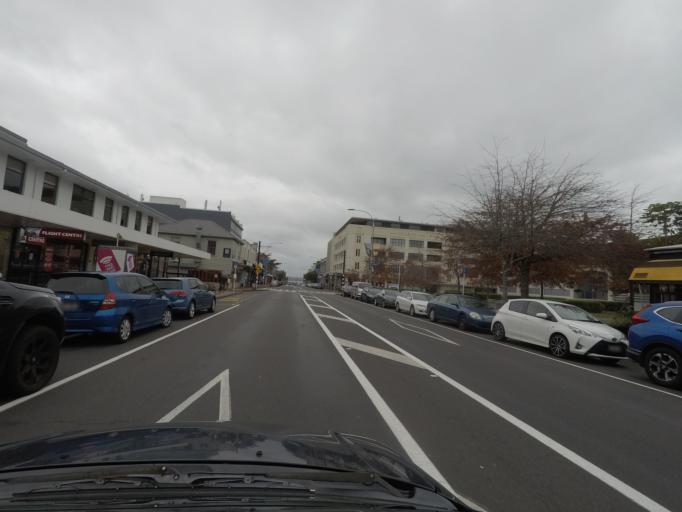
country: NZ
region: Auckland
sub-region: Auckland
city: Auckland
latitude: -36.8547
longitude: 174.7800
